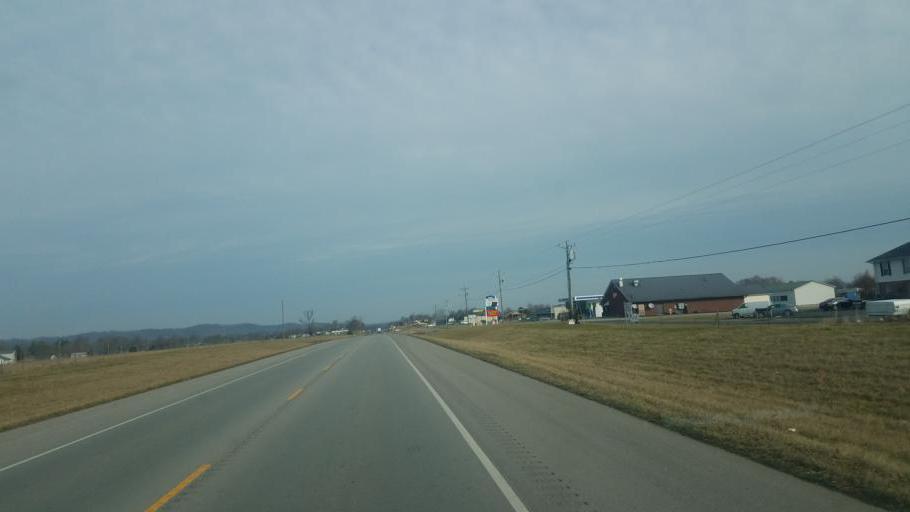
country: US
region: Kentucky
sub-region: Boyle County
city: Junction City
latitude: 37.5144
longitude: -84.8067
